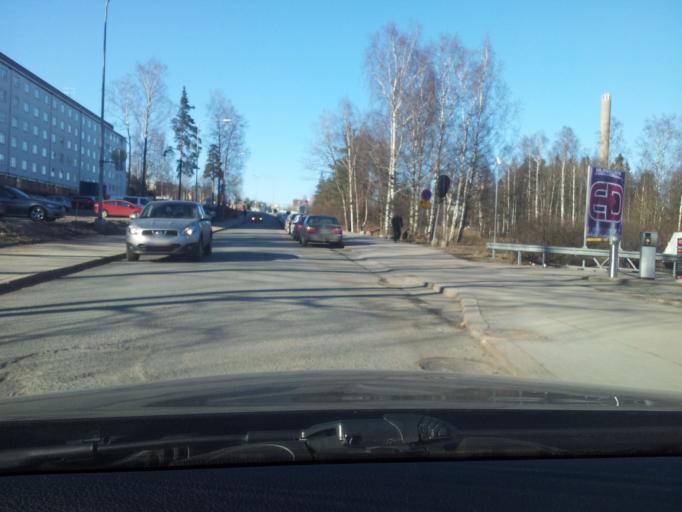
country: FI
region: Uusimaa
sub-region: Helsinki
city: Vantaa
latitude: 60.2216
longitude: 25.0785
